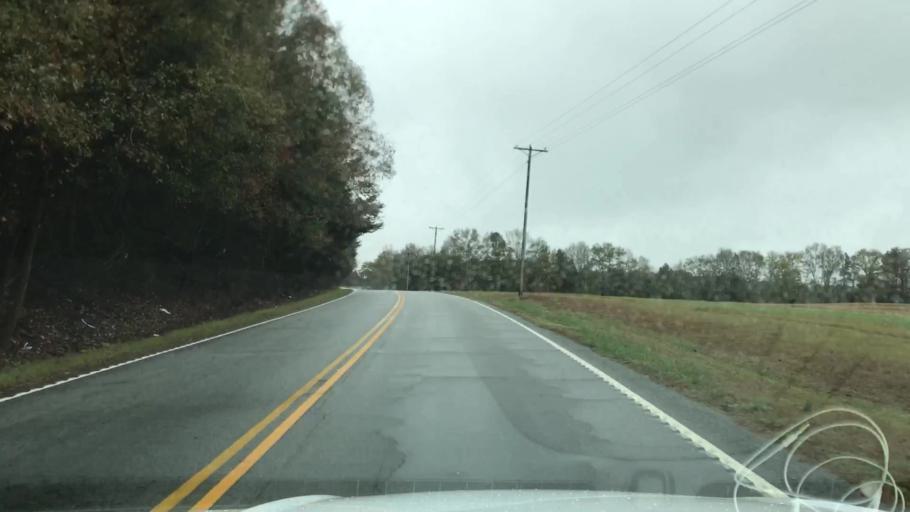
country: US
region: South Carolina
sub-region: Spartanburg County
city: Roebuck
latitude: 34.8228
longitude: -81.9240
